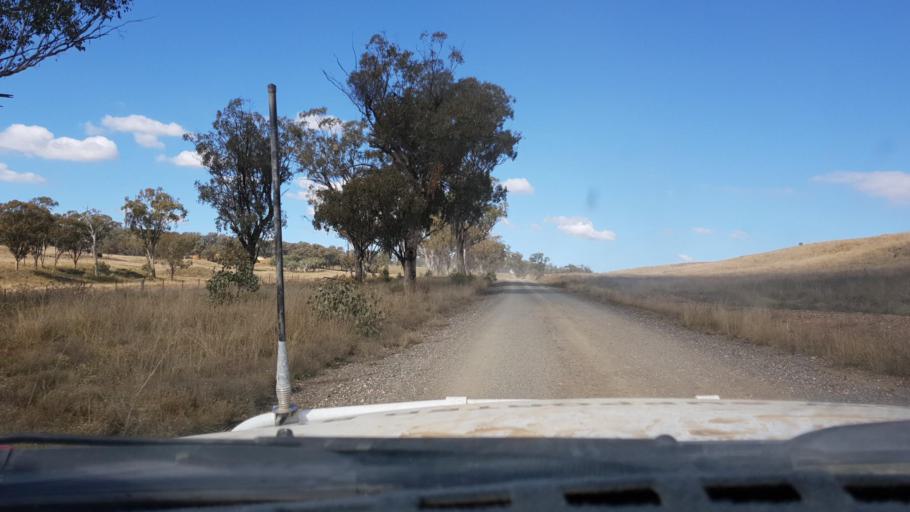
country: AU
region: New South Wales
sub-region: Tamworth Municipality
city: Manilla
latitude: -30.4570
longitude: 150.7417
